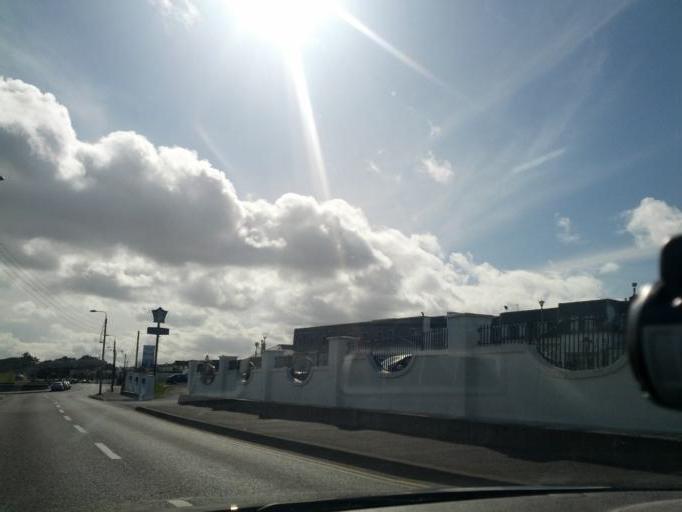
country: IE
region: Leinster
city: Portmarnock
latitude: 53.4357
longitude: -6.1229
